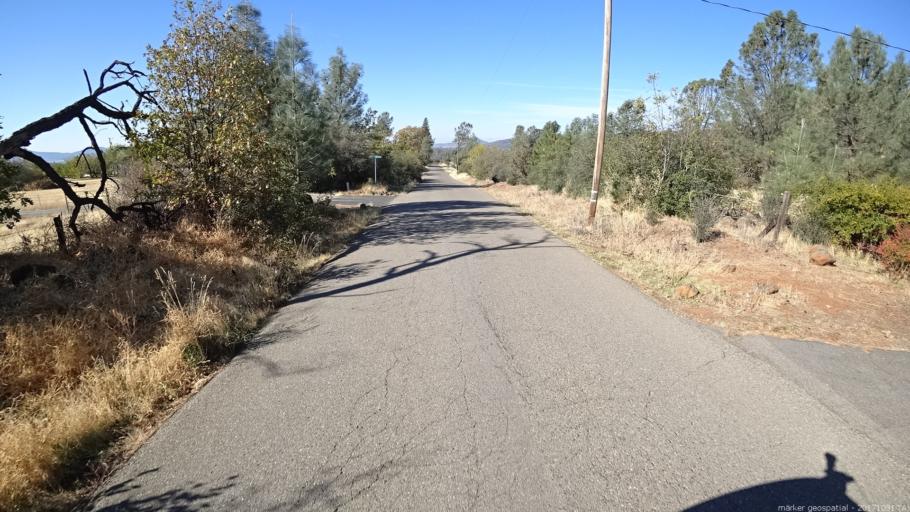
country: US
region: California
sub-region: Shasta County
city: Shingletown
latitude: 40.4463
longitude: -121.8555
